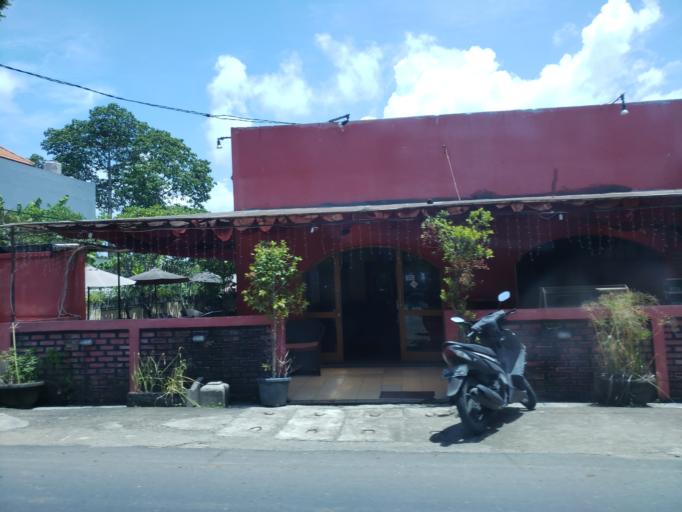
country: ID
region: Bali
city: Jimbaran
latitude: -8.7911
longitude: 115.1639
